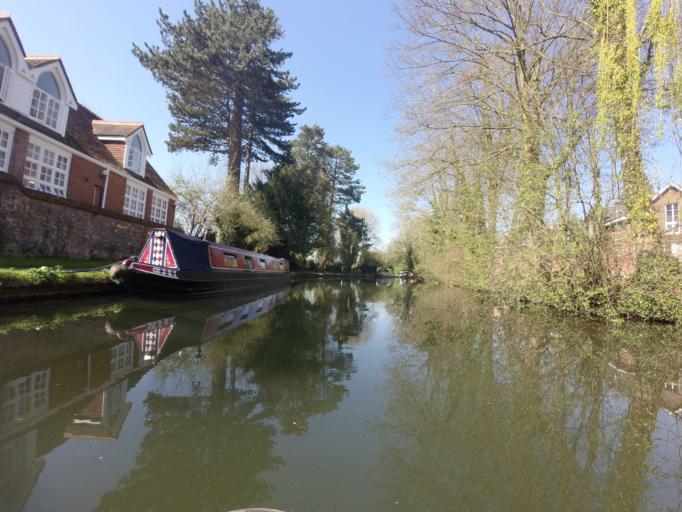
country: GB
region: England
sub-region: Hertfordshire
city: Abbots Langley
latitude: 51.6937
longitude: -0.4367
